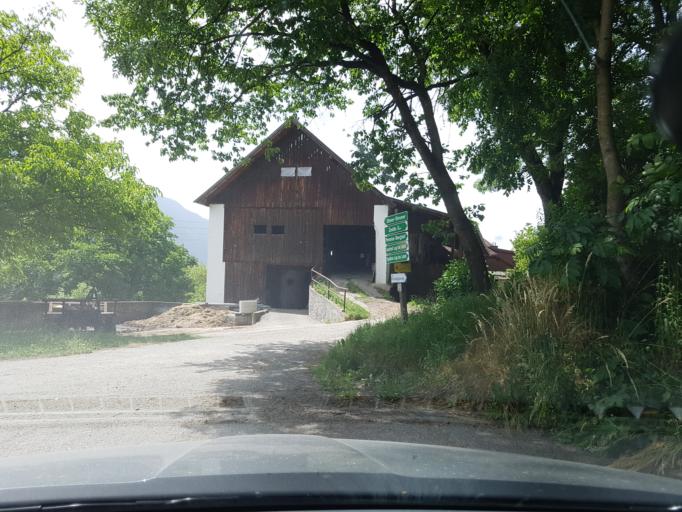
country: AT
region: Carinthia
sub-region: Politischer Bezirk Spittal an der Drau
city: Millstatt
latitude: 46.7803
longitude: 13.5479
